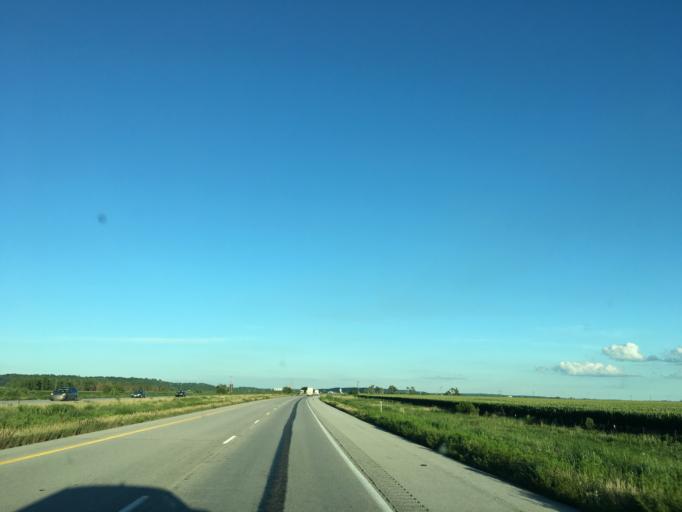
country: US
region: Iowa
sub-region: Fremont County
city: Hamburg
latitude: 40.6284
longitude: -95.7150
